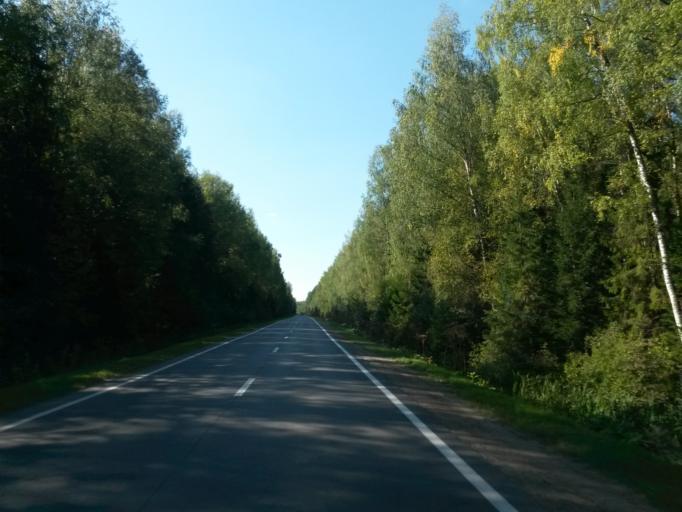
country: RU
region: Jaroslavl
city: Yaroslavl
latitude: 57.8015
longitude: 39.7929
